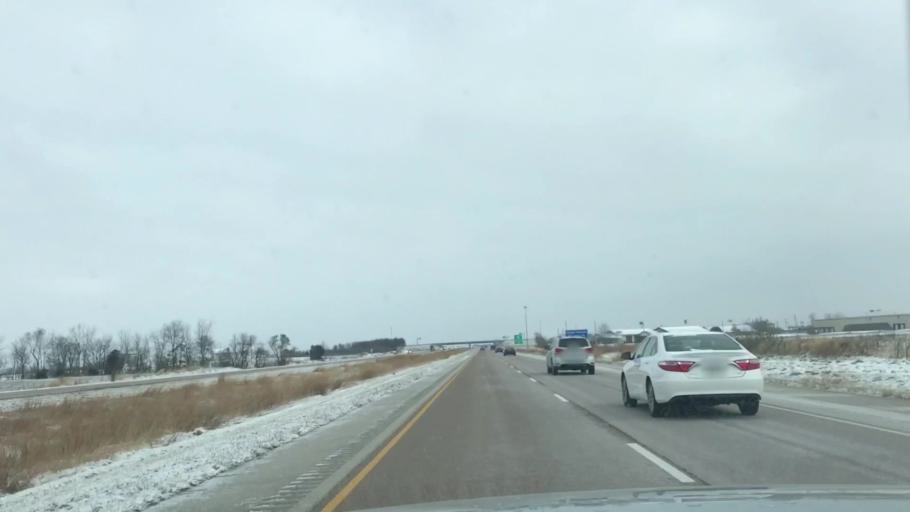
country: US
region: Illinois
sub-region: Montgomery County
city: Litchfield
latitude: 39.1668
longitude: -89.6867
